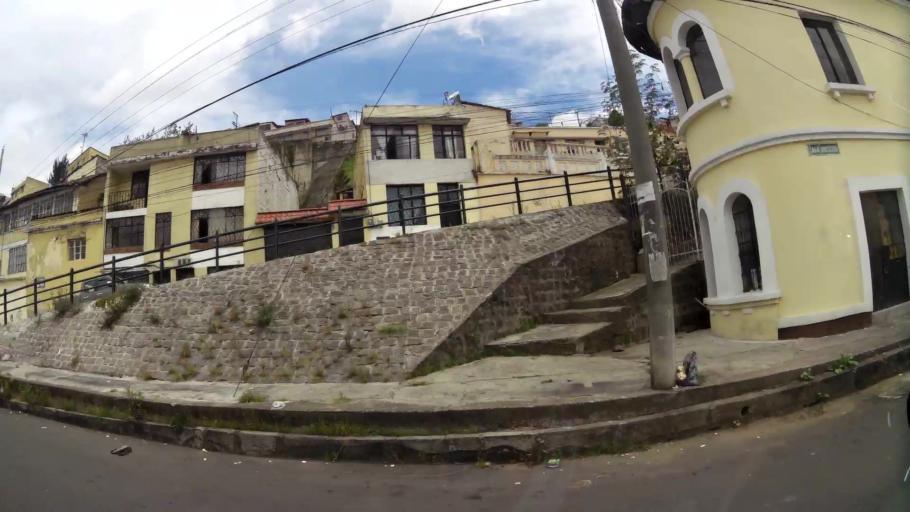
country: EC
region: Pichincha
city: Quito
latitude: -0.2156
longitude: -78.5194
